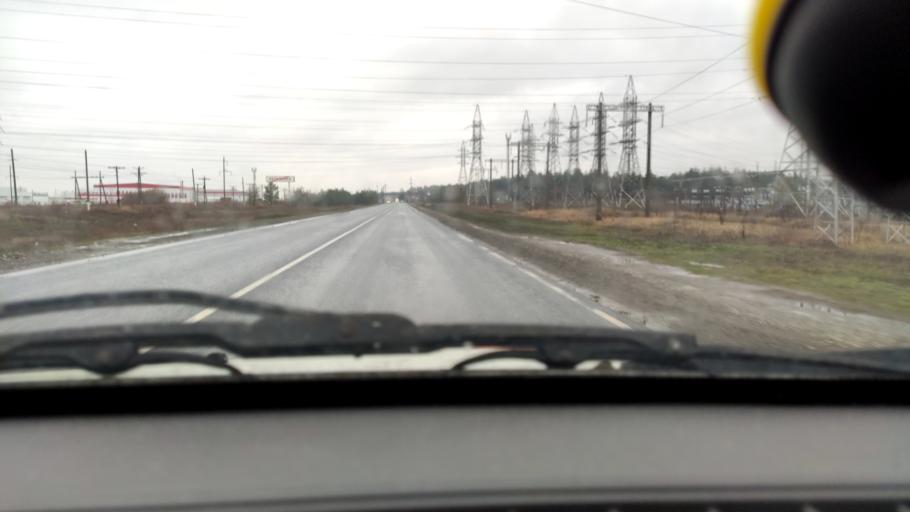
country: RU
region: Samara
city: Zhigulevsk
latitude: 53.5600
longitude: 49.5397
